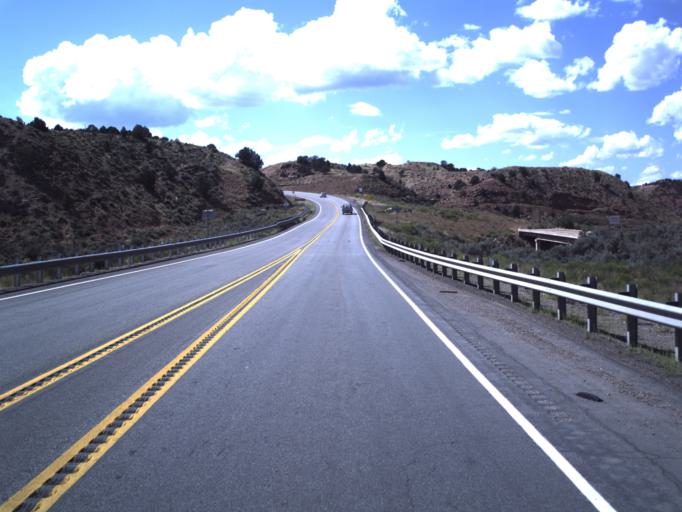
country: US
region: Utah
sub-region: Duchesne County
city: Duchesne
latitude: 40.2002
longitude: -110.7831
